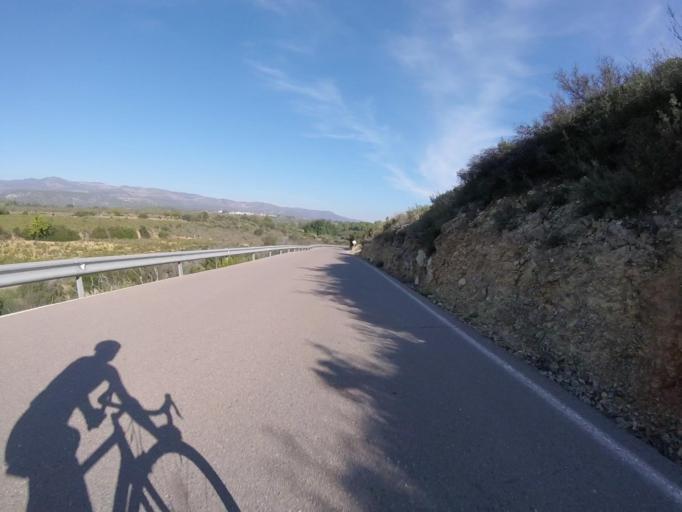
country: ES
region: Valencia
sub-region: Provincia de Castello
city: Benlloch
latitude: 40.2491
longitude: 0.0766
